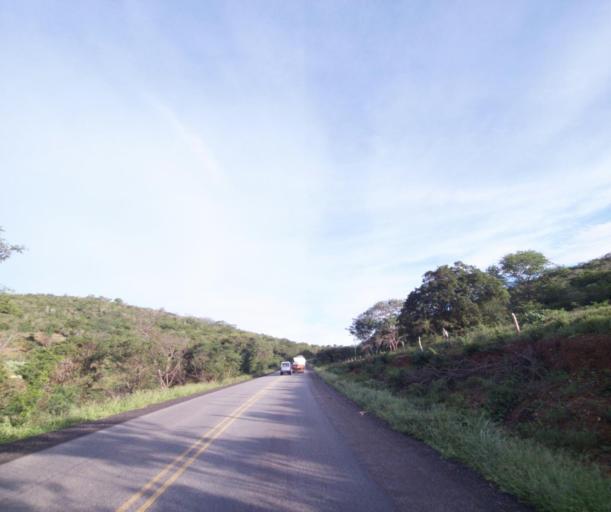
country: BR
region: Bahia
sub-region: Cacule
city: Cacule
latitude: -14.1939
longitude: -42.1433
